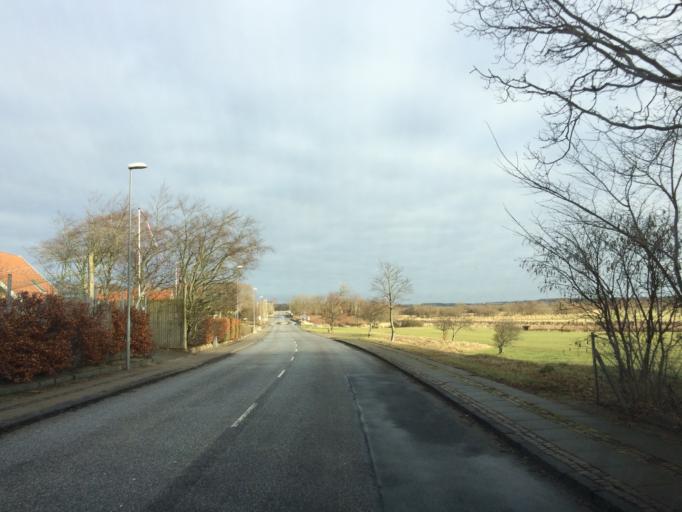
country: DK
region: Central Jutland
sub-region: Holstebro Kommune
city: Ulfborg
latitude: 56.3415
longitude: 8.3491
